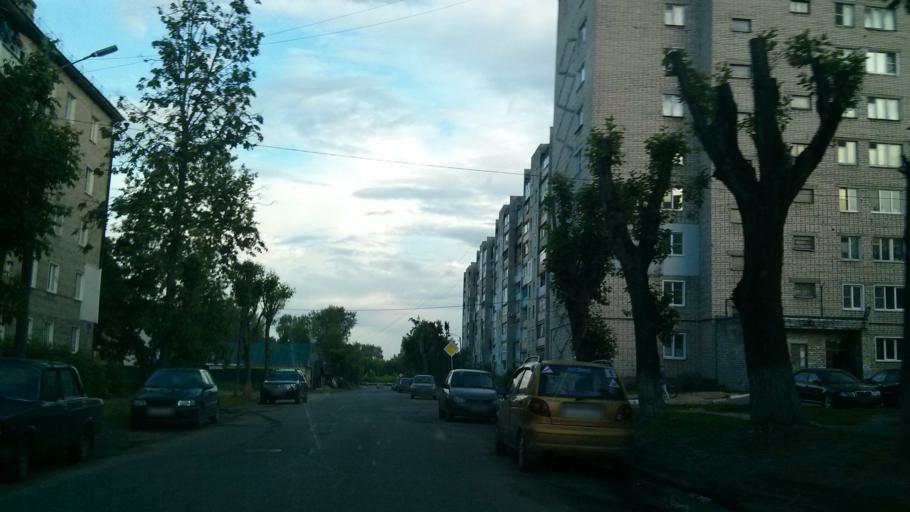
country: RU
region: Vladimir
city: Murom
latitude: 55.5680
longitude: 42.0510
